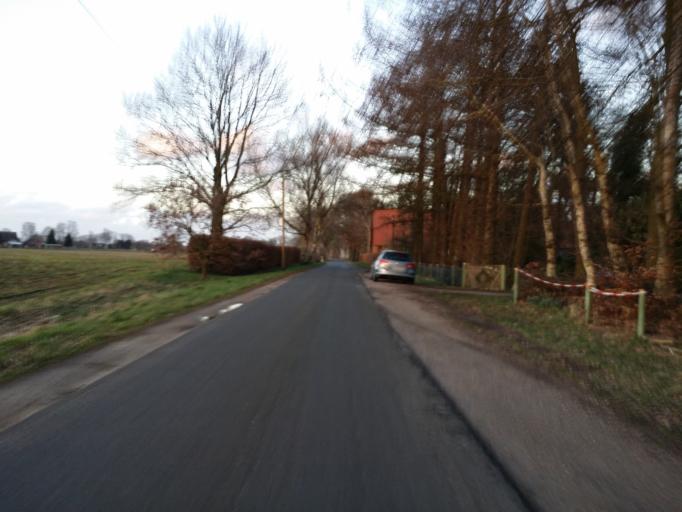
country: DE
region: Lower Saxony
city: Delmenhorst
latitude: 53.0119
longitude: 8.6146
